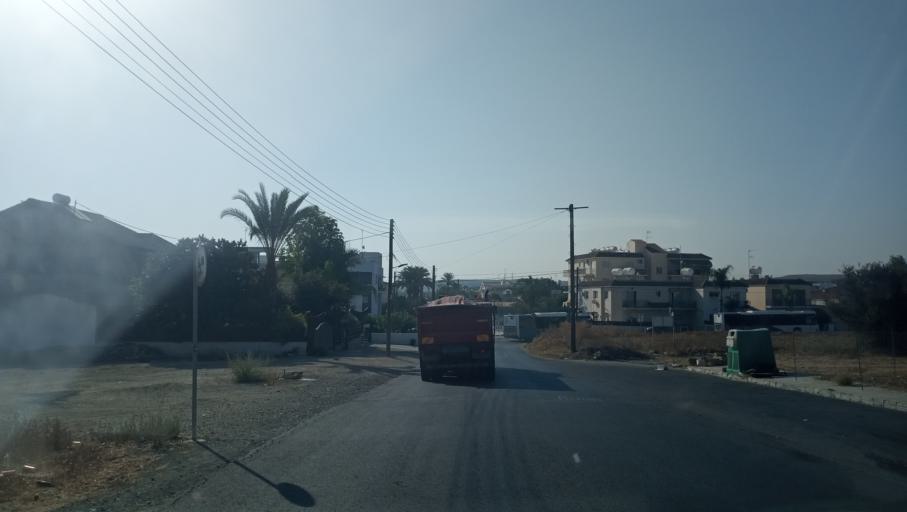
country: CY
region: Lefkosia
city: Geri
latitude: 35.1127
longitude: 33.4270
